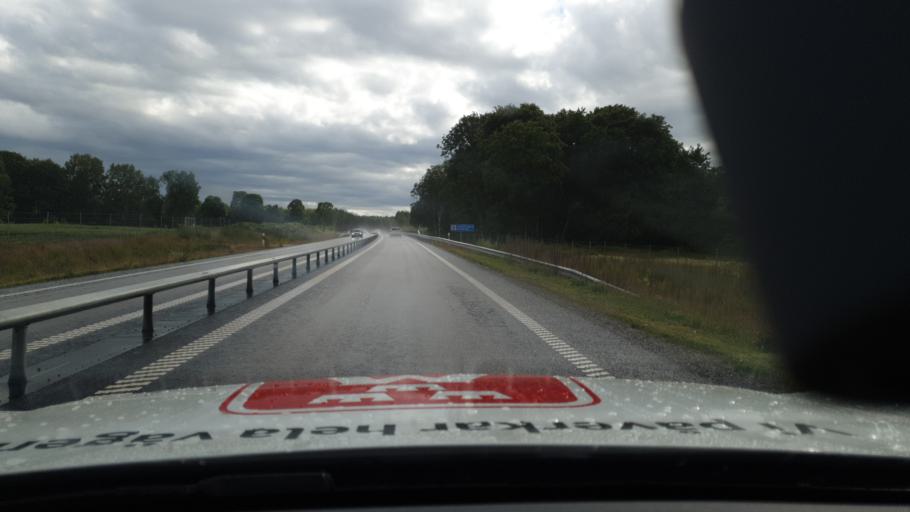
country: SE
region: Vaestra Goetaland
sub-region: Lidkopings Kommun
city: Vinninga
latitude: 58.4870
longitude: 13.2829
